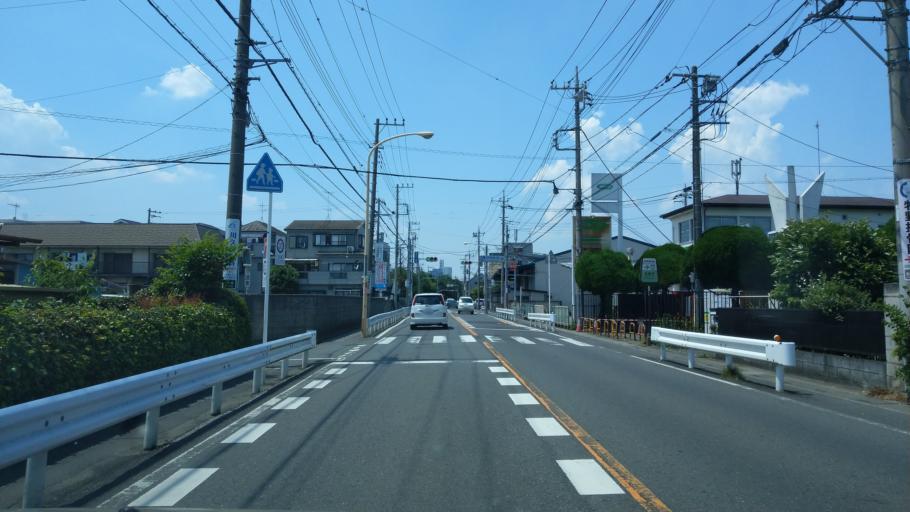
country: JP
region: Saitama
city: Yono
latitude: 35.8720
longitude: 139.6617
